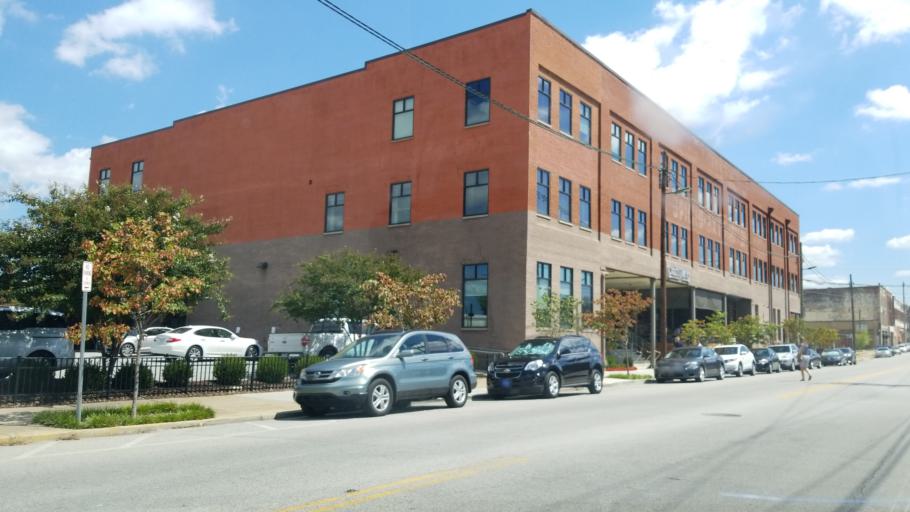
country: US
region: Tennessee
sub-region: Hamilton County
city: Chattanooga
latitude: 35.0372
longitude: -85.3102
